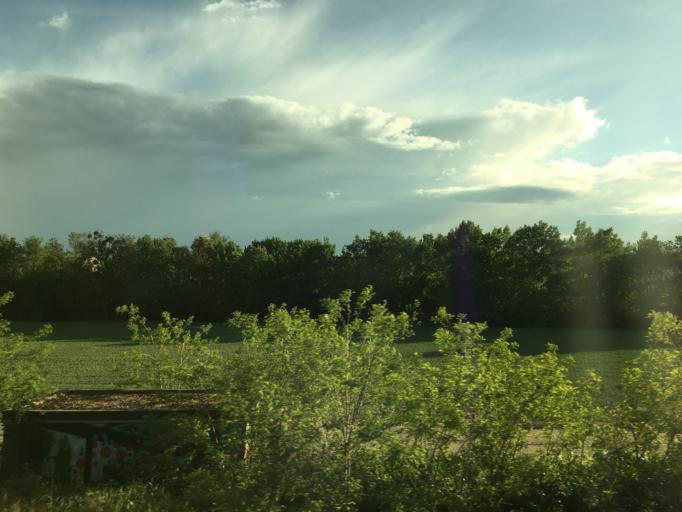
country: DE
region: Saxony
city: Dresden
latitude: 51.0801
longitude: 13.7282
